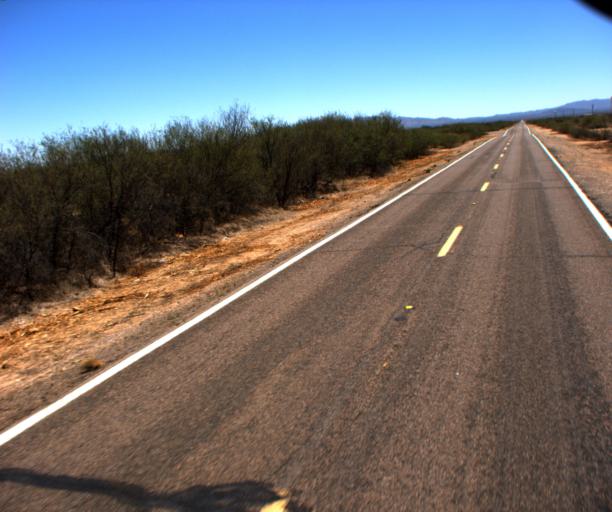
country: US
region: Arizona
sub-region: Pima County
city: Ajo
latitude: 32.1936
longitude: -112.4402
